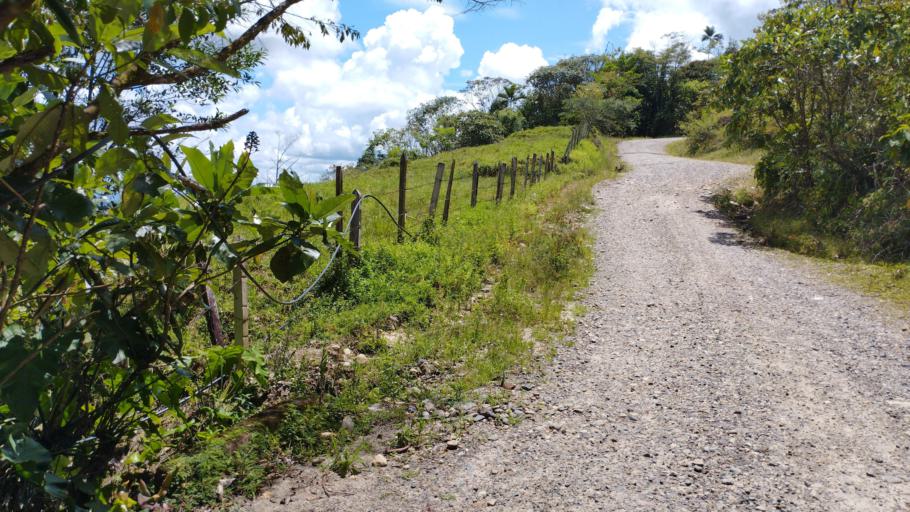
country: CO
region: Boyaca
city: San Luis de Gaceno
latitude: 4.7510
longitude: -73.1391
